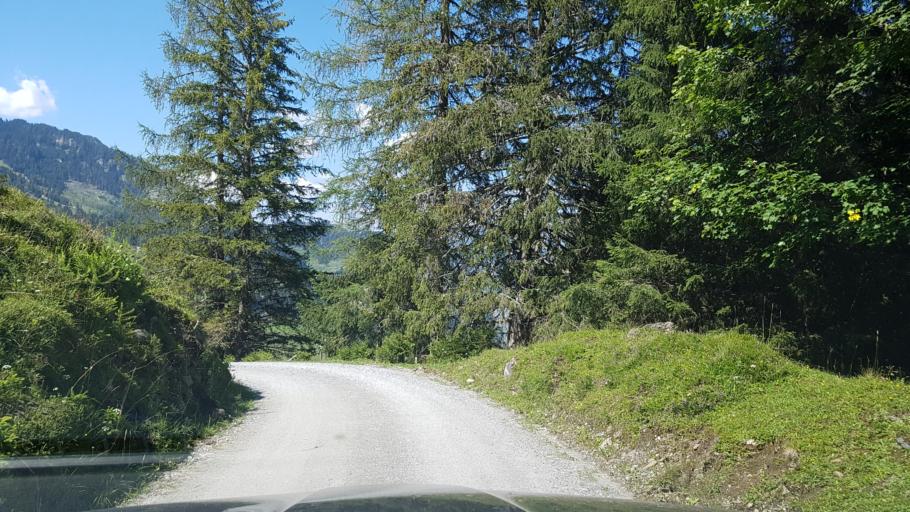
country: AT
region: Salzburg
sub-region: Politischer Bezirk Sankt Johann im Pongau
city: Dorfgastein
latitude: 47.2484
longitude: 13.0738
